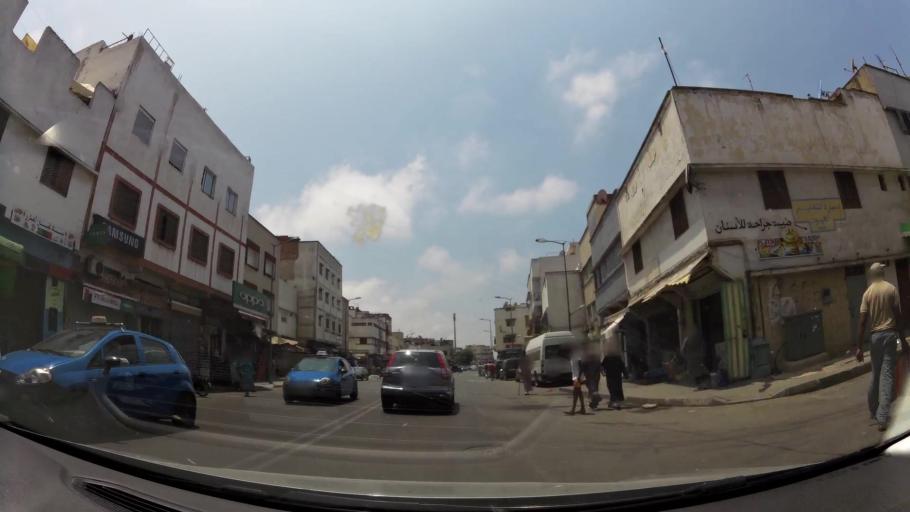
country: MA
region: Rabat-Sale-Zemmour-Zaer
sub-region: Rabat
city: Rabat
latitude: 33.9823
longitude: -6.8810
